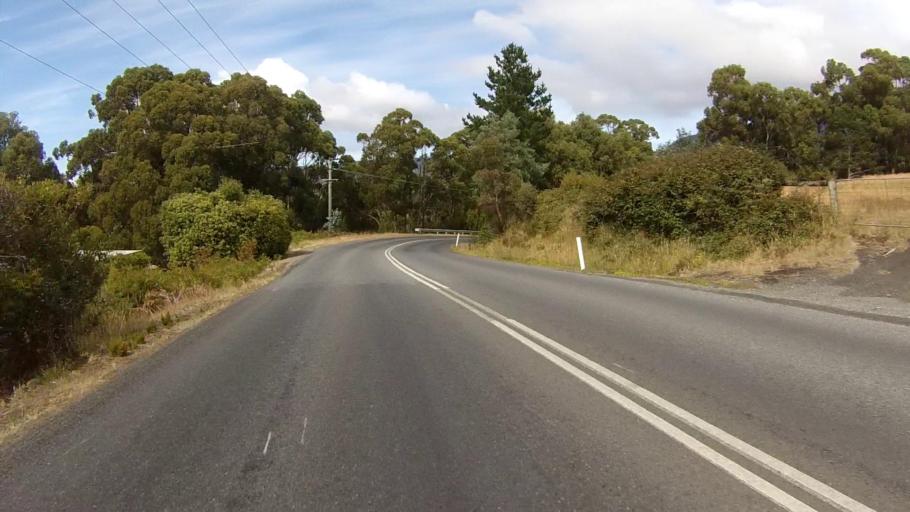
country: AU
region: Tasmania
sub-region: Kingborough
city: Kettering
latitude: -43.1469
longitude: 147.2418
